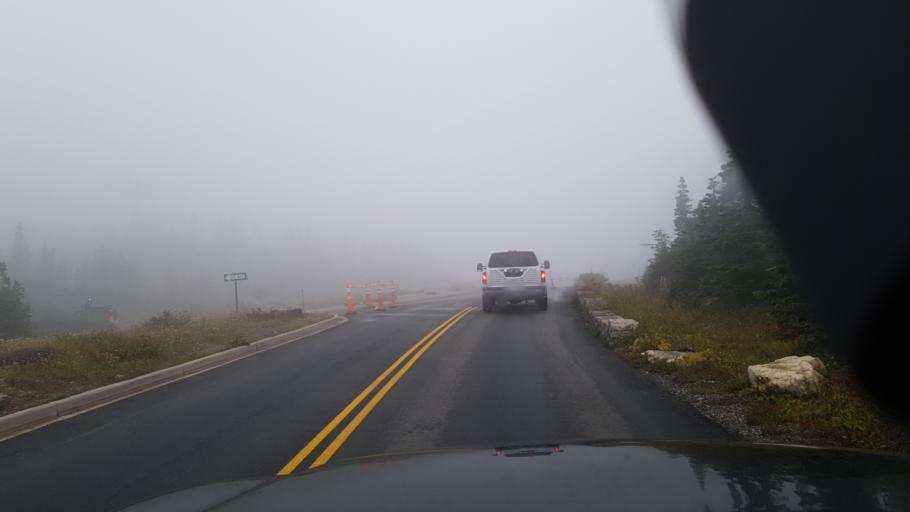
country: US
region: Montana
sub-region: Flathead County
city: Columbia Falls
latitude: 48.6963
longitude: -113.7173
